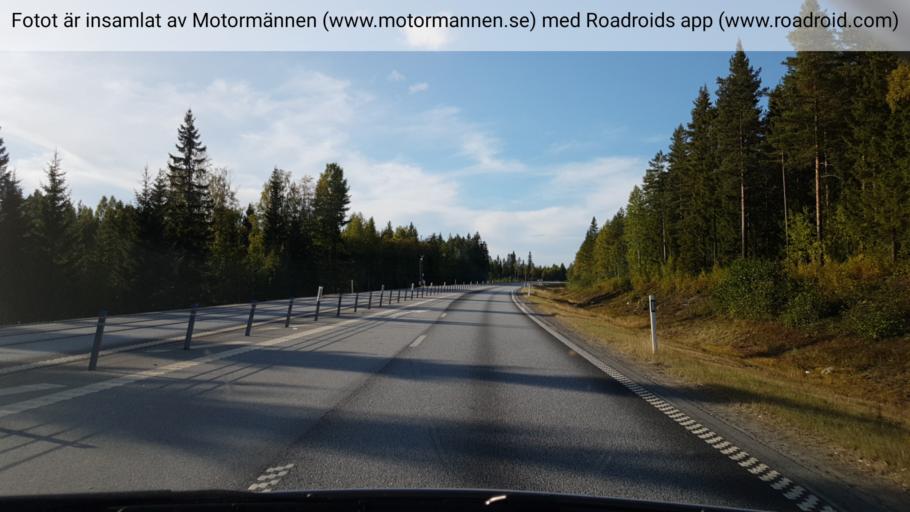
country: SE
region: Vaesterbotten
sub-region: Vannas Kommun
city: Vannasby
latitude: 63.9013
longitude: 19.8995
